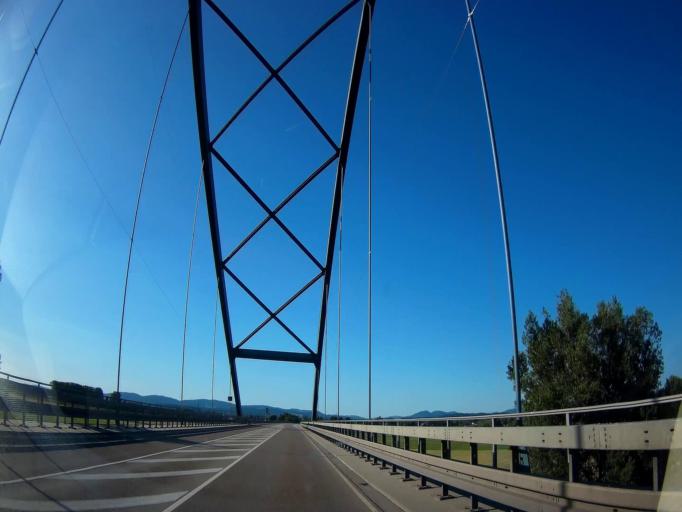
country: DE
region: Bavaria
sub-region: Lower Bavaria
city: Parkstetten
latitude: 48.8976
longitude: 12.6159
